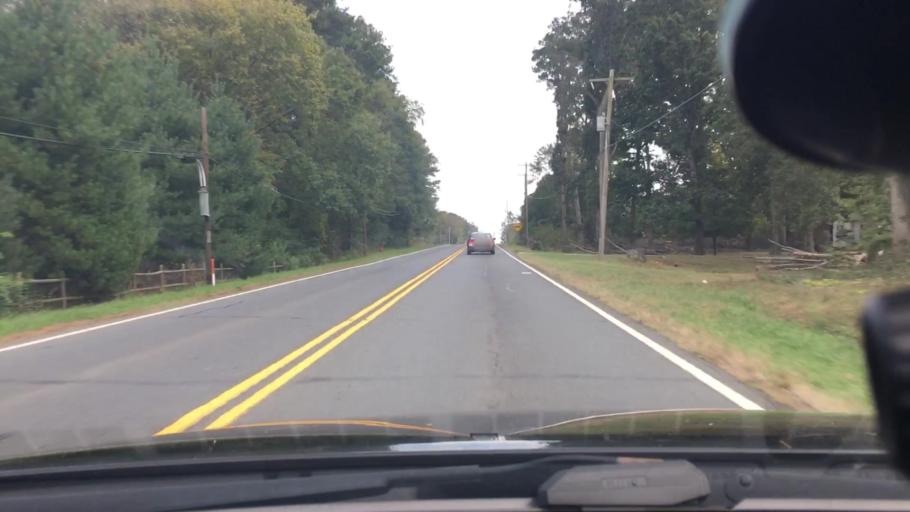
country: US
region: North Carolina
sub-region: Stanly County
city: Albemarle
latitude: 35.3265
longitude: -80.1312
